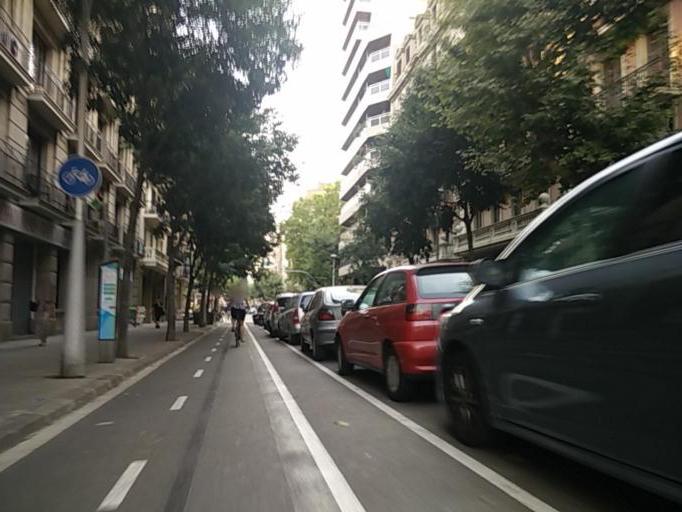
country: ES
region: Catalonia
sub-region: Provincia de Barcelona
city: Gracia
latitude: 41.4008
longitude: 2.1697
